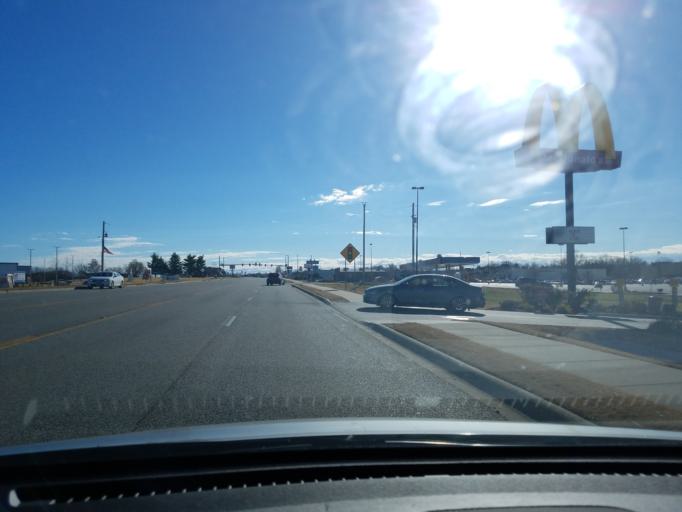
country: US
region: Arkansas
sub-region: Carroll County
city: Berryville
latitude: 36.3789
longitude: -93.5872
